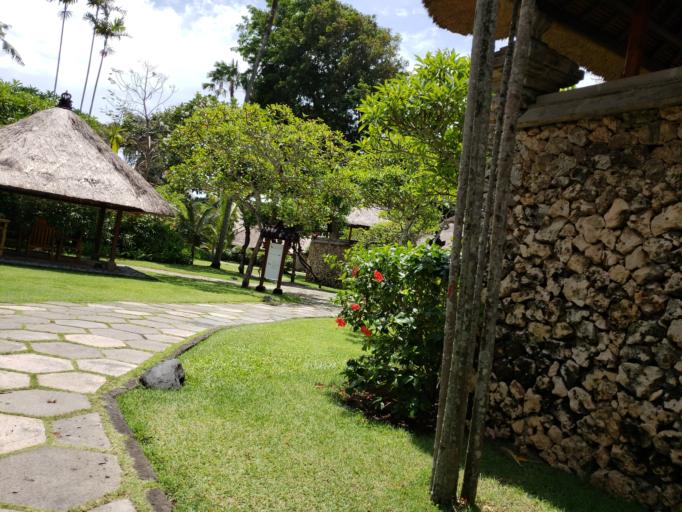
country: ID
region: Bali
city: Kuta
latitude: -8.6894
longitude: 115.1572
